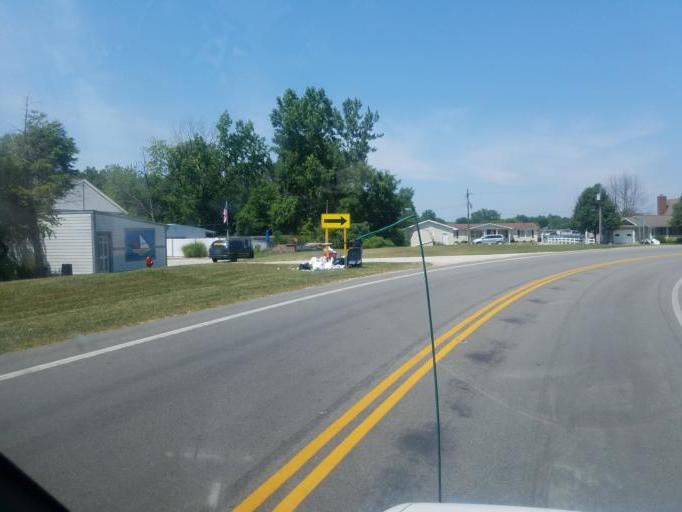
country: US
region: Ohio
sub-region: Auglaize County
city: Saint Marys
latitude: 40.5089
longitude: -84.4344
